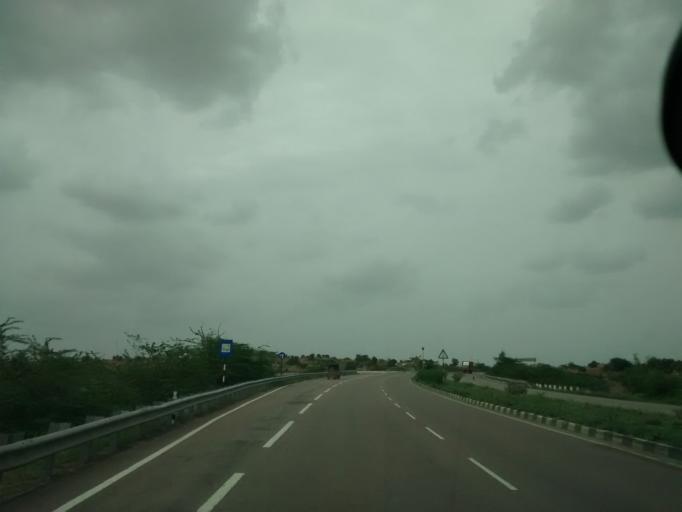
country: IN
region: Andhra Pradesh
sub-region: Kurnool
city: Ramapuram
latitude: 15.1530
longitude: 77.6669
